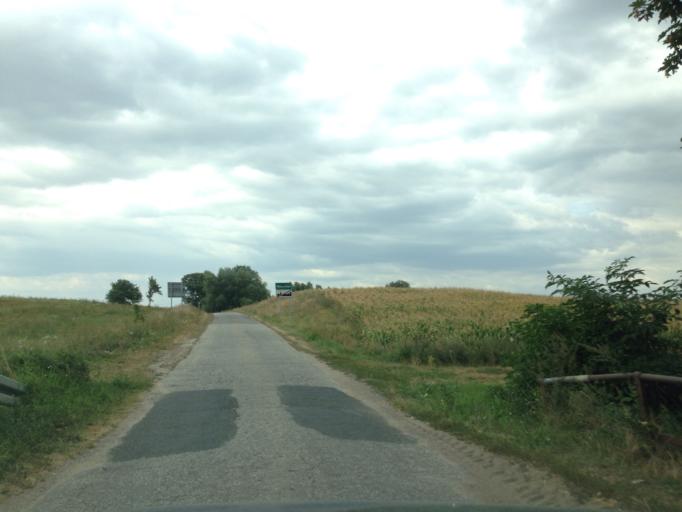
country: PL
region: Kujawsko-Pomorskie
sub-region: Powiat wabrzeski
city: Pluznica
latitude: 53.2092
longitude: 18.7841
